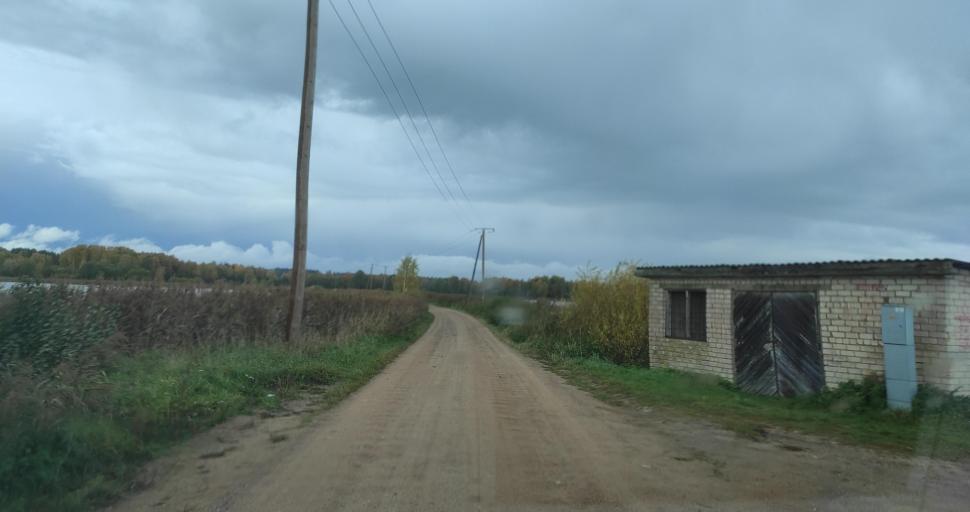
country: LV
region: Skrunda
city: Skrunda
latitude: 56.6856
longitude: 21.9902
